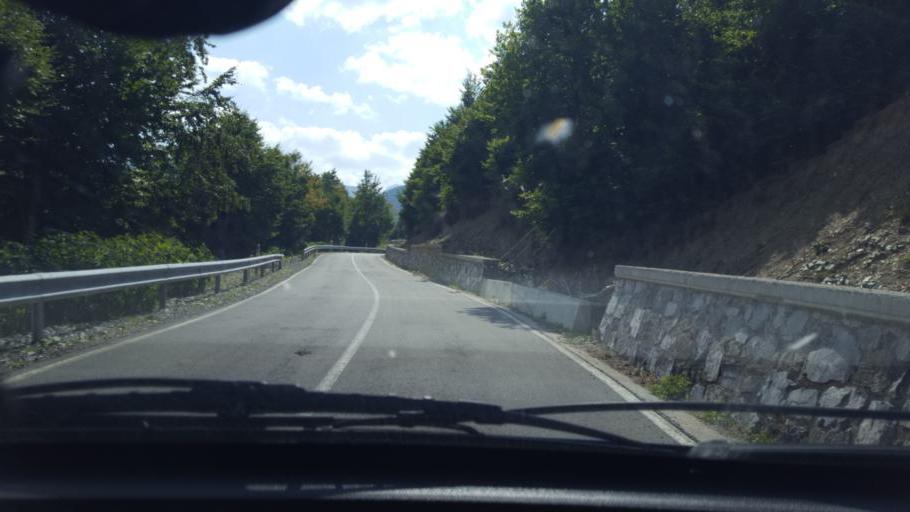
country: AL
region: Kukes
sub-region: Rrethi i Tropojes
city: Valbone
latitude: 42.5373
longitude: 19.7208
